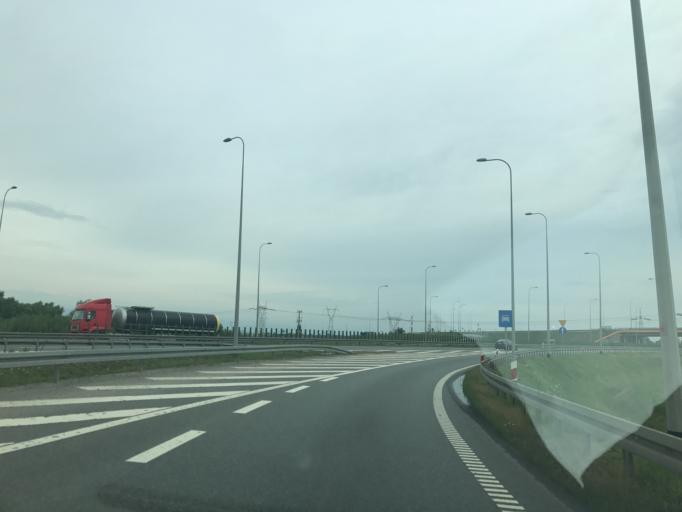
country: PL
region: Pomeranian Voivodeship
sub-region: Gdansk
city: Gdansk
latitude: 54.3180
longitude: 18.7020
